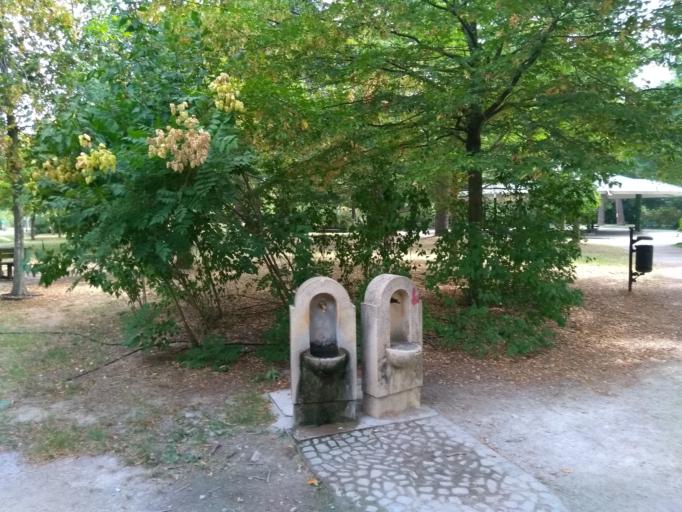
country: IT
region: Emilia-Romagna
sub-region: Provincia di Bologna
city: Imola
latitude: 44.3415
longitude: 11.7061
